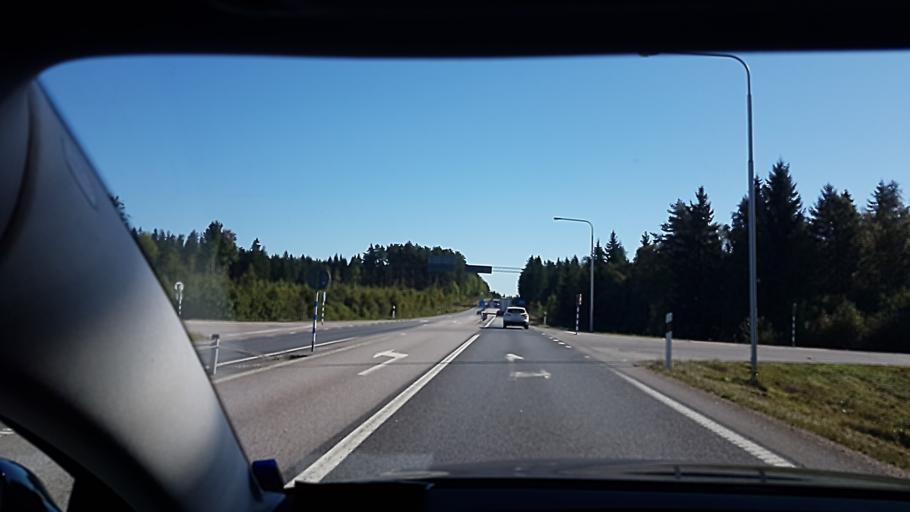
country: SE
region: Kronoberg
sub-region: Vaxjo Kommun
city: Ingelstad
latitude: 56.8695
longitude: 14.9753
